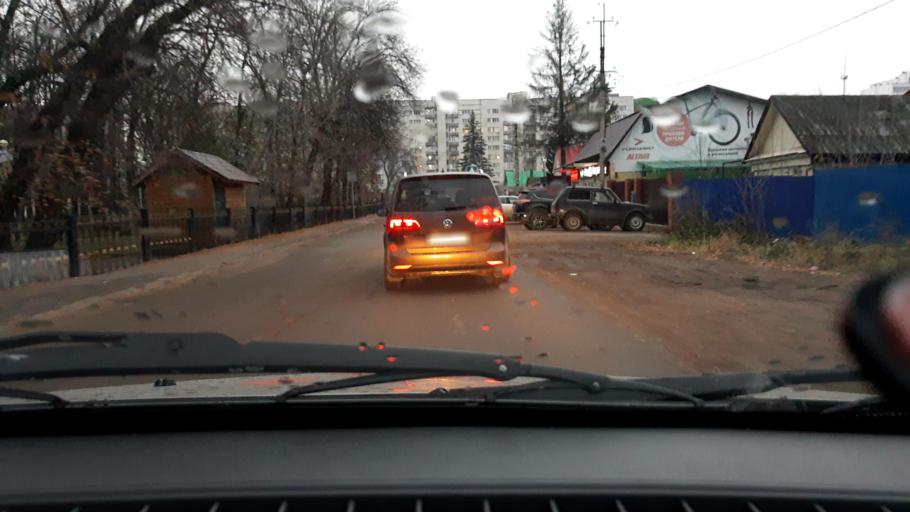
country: RU
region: Bashkortostan
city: Avdon
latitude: 54.7037
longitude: 55.8255
